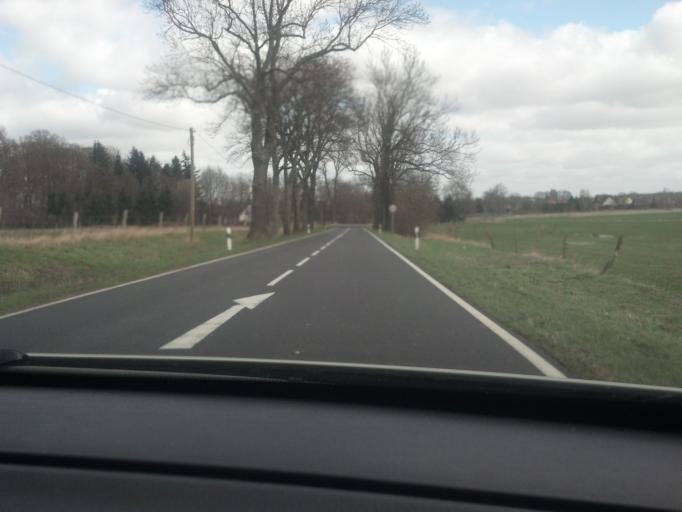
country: DE
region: Brandenburg
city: Gerdshagen
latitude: 53.3052
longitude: 12.2276
